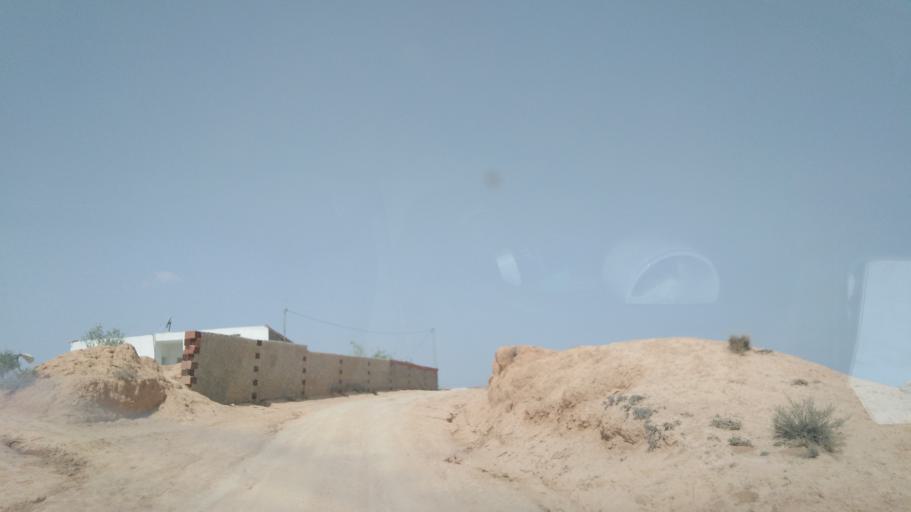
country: TN
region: Safaqis
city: Sfax
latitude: 34.6409
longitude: 10.5626
